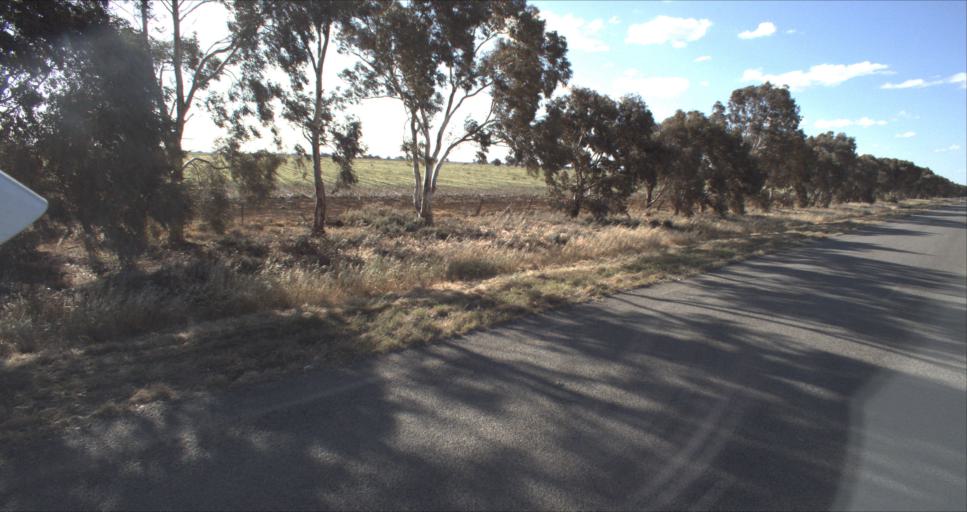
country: AU
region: New South Wales
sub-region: Leeton
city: Leeton
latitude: -34.5516
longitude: 146.2790
